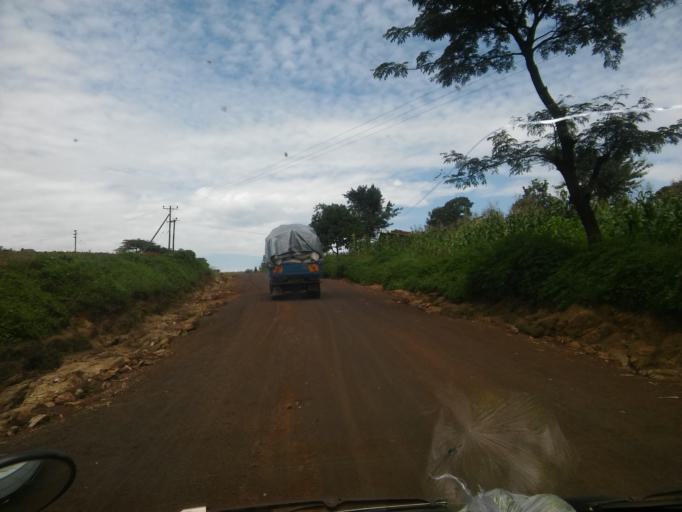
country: UG
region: Eastern Region
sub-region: Tororo District
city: Tororo
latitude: 0.8150
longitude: 34.3014
